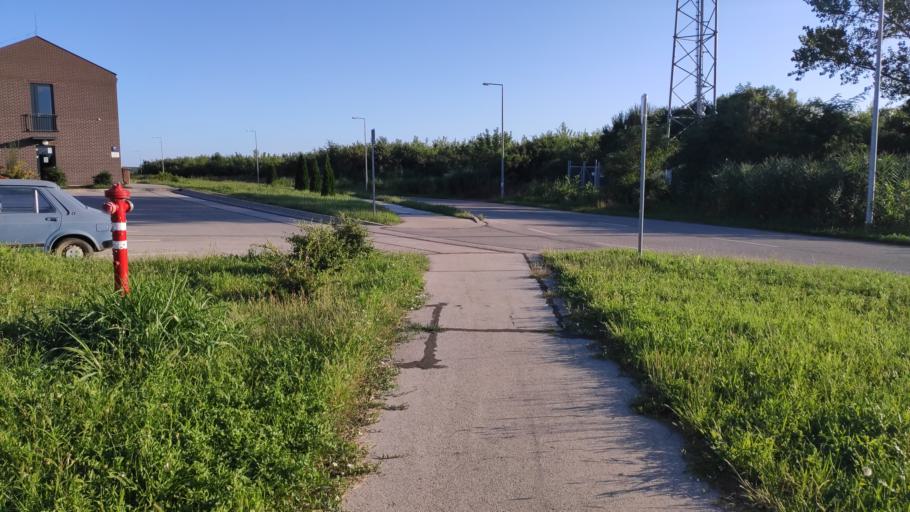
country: HU
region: Bekes
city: Mezobereny
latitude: 46.7573
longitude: 21.0376
